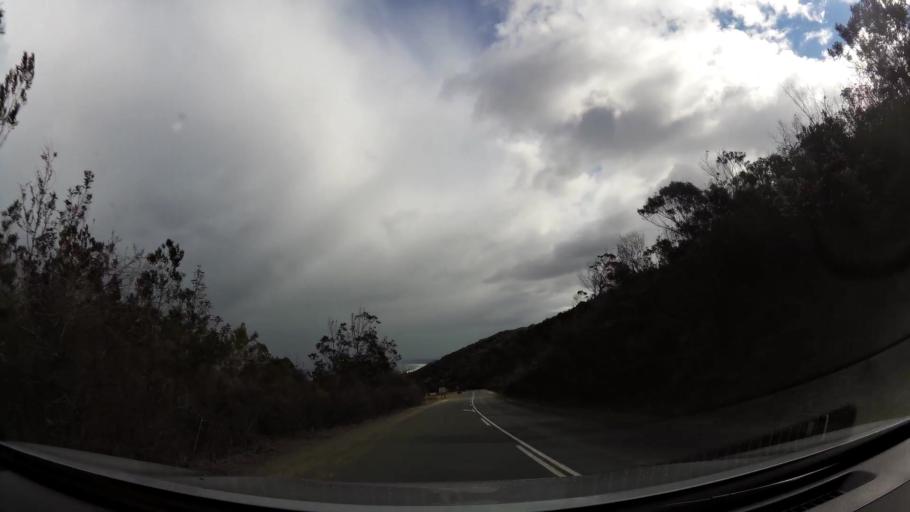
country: ZA
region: Western Cape
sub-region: Eden District Municipality
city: George
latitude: -34.0459
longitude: 22.3163
